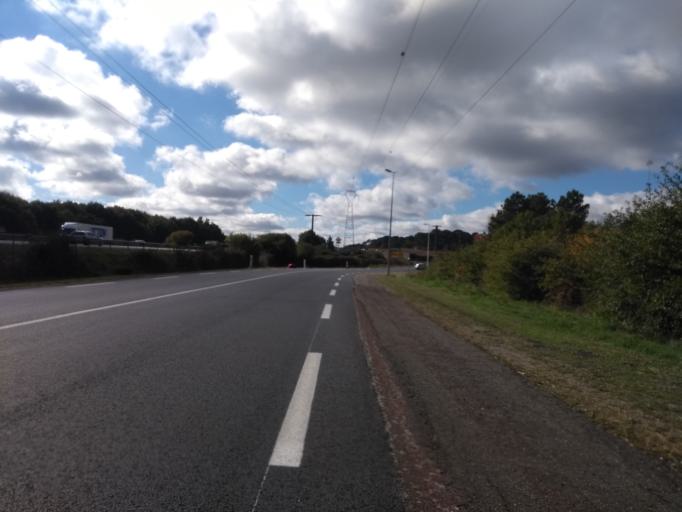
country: FR
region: Aquitaine
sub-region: Departement de la Gironde
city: Cestas
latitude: 44.7603
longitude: -0.6805
